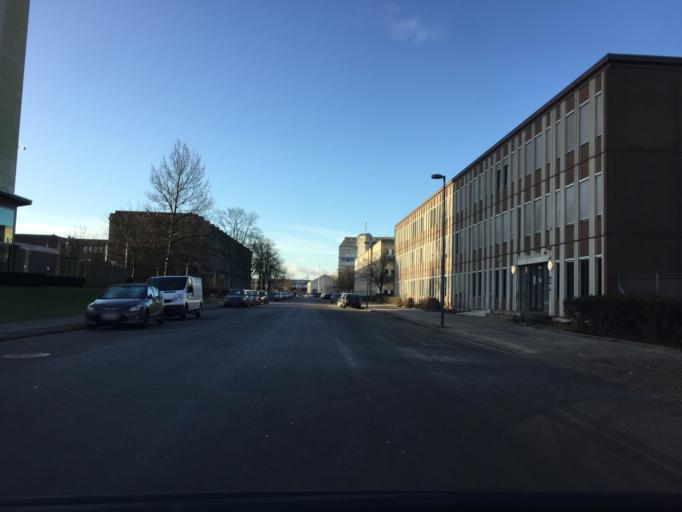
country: DK
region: Capital Region
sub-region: Kobenhavn
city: Vanlose
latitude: 55.6594
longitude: 12.5081
